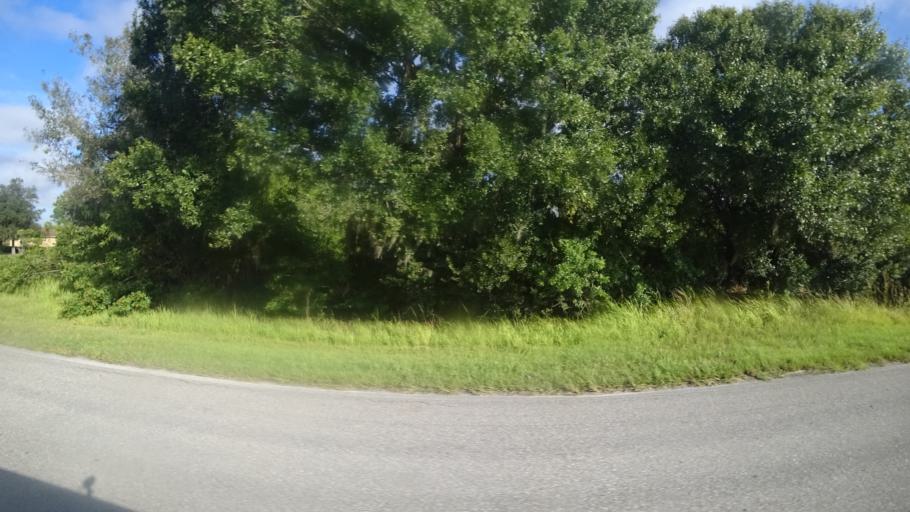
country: US
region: Florida
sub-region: Manatee County
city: Ellenton
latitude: 27.5574
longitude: -82.4073
